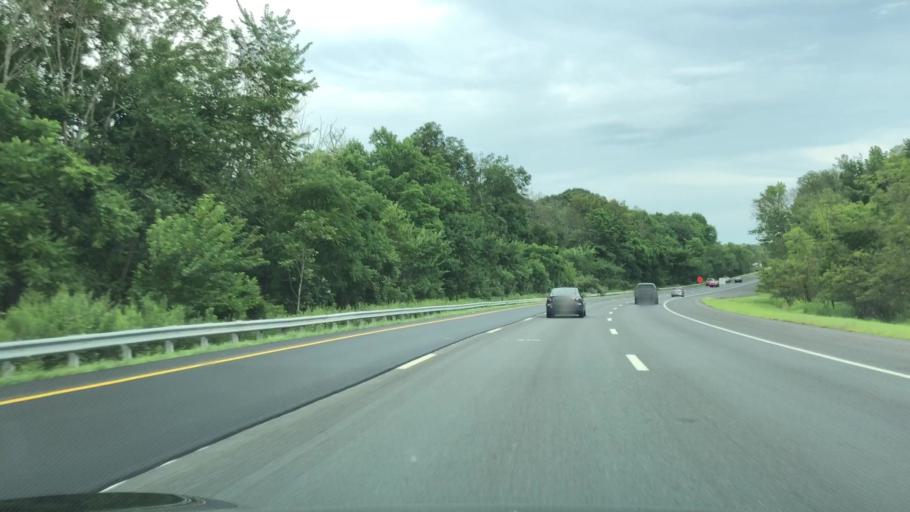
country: US
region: New Jersey
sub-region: Mercer County
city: Ewing
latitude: 40.2917
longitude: -74.7710
